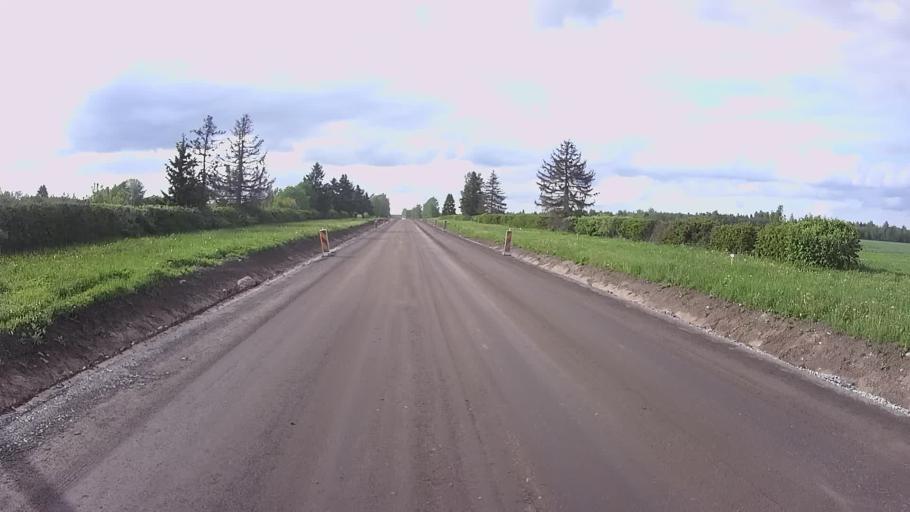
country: EE
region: Jogevamaa
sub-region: Mustvee linn
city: Mustvee
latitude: 59.0193
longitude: 26.7039
